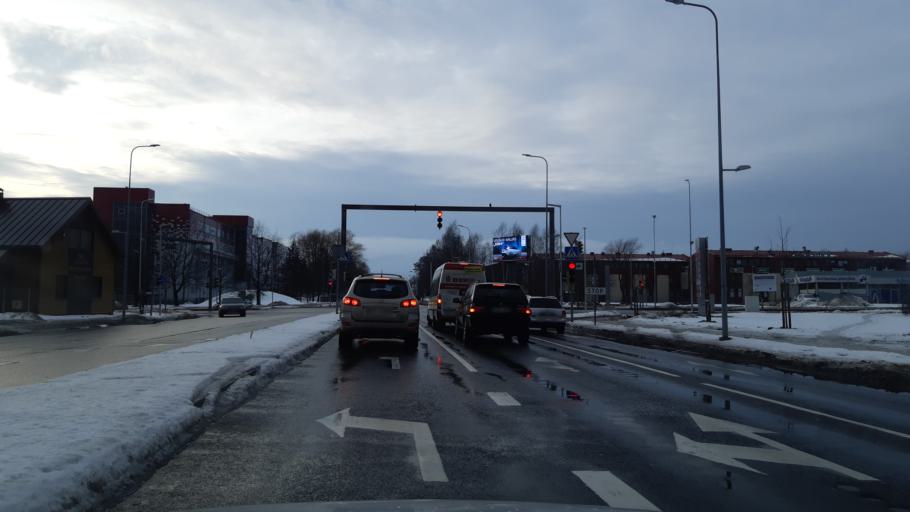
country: LT
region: Kauno apskritis
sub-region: Kaunas
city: Aleksotas
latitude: 54.8750
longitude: 23.8925
